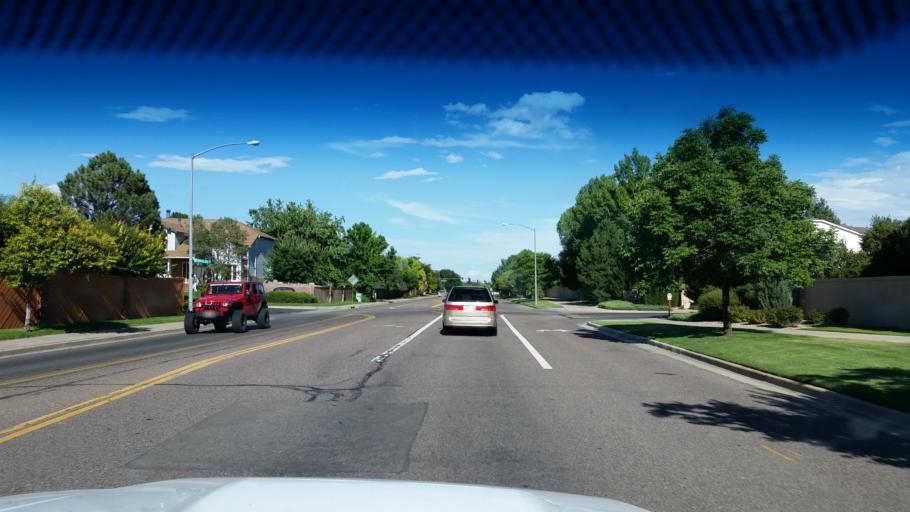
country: US
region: Colorado
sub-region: Adams County
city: Northglenn
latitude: 39.9284
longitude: -104.9632
